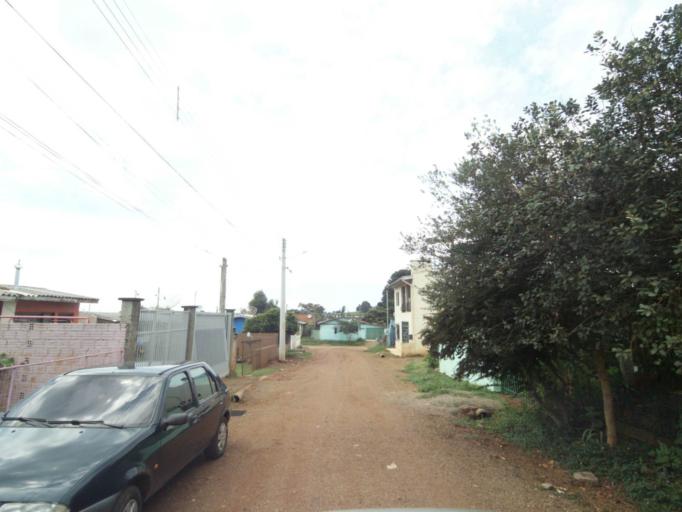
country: BR
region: Rio Grande do Sul
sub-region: Lagoa Vermelha
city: Lagoa Vermelha
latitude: -28.2234
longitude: -51.5142
